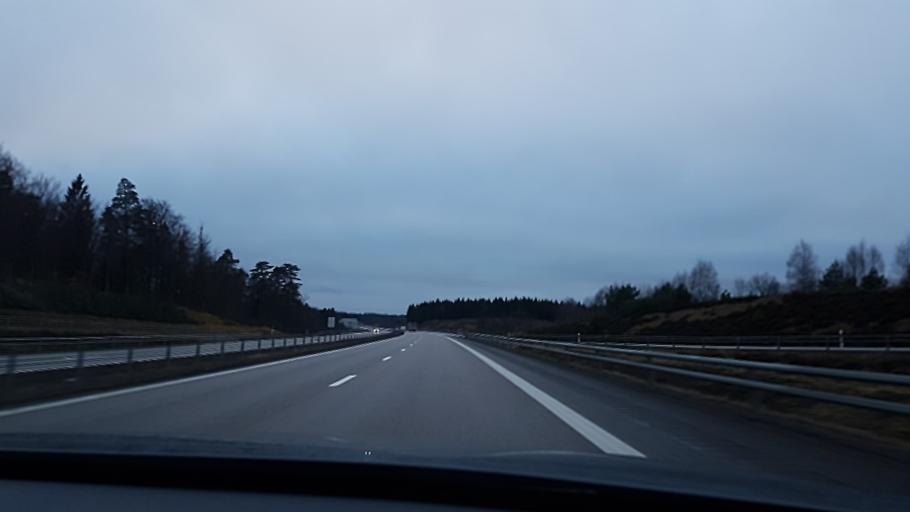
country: SE
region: Skane
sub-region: Orkelljunga Kommun
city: OErkelljunga
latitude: 56.2833
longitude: 13.3399
